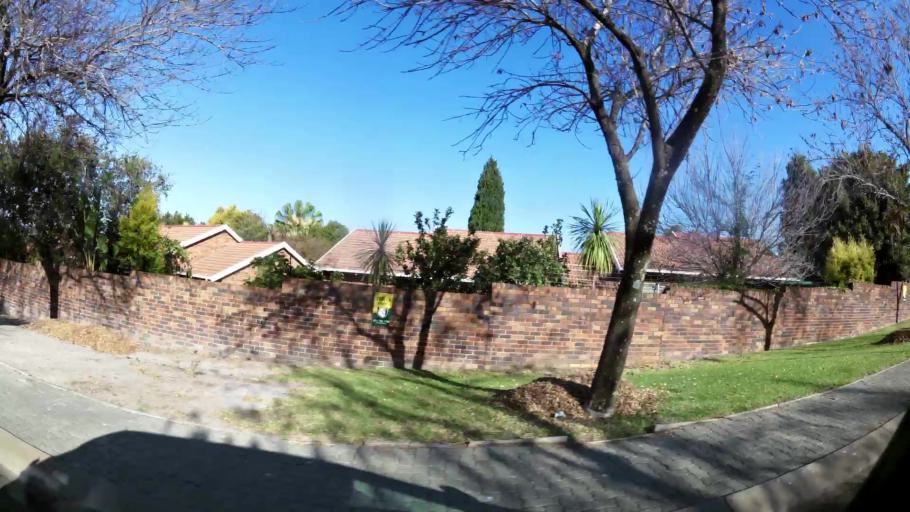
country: ZA
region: Gauteng
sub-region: City of Johannesburg Metropolitan Municipality
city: Roodepoort
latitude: -26.0888
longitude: 27.9601
